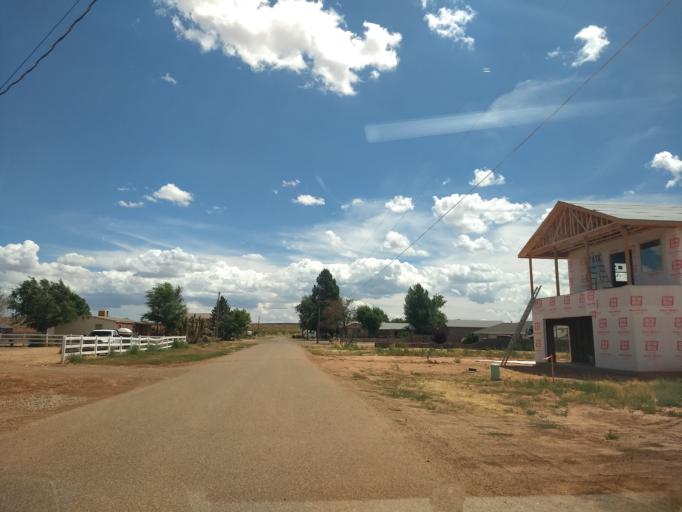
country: US
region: Arizona
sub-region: Coconino County
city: Fredonia
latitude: 36.9473
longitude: -112.5206
